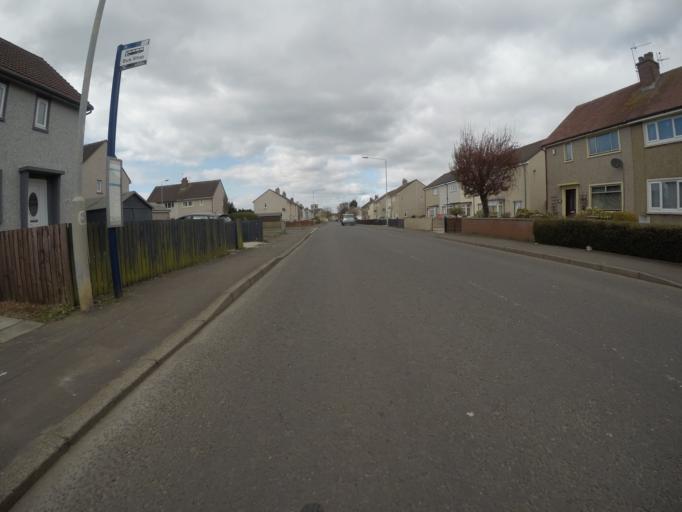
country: GB
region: Scotland
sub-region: North Ayrshire
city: Irvine
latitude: 55.6233
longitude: -4.6572
